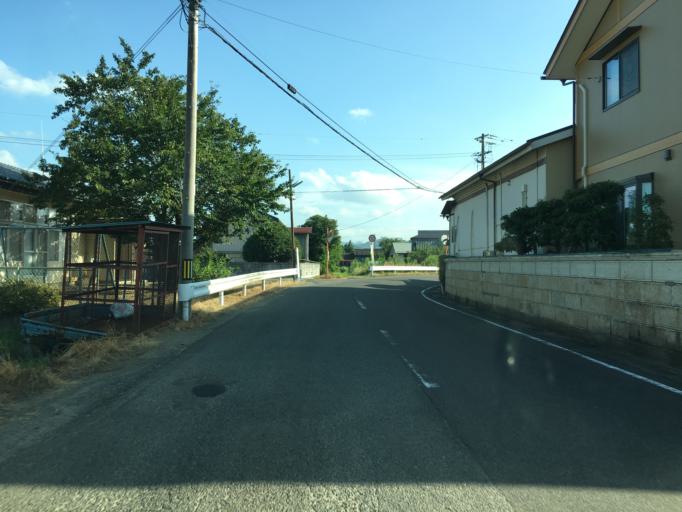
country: JP
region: Fukushima
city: Yanagawamachi-saiwaicho
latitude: 37.8354
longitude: 140.5845
